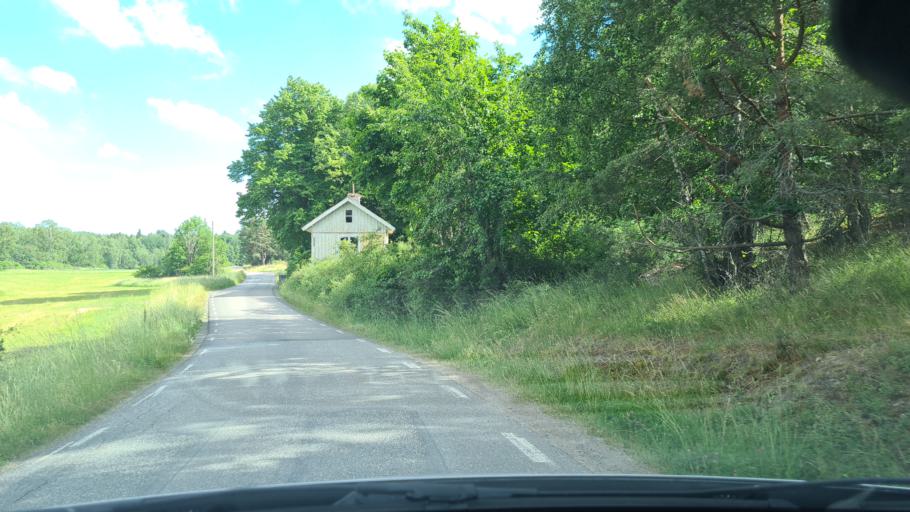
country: SE
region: Stockholm
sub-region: Varmdo Kommun
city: Mortnas
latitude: 59.4088
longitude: 18.4541
